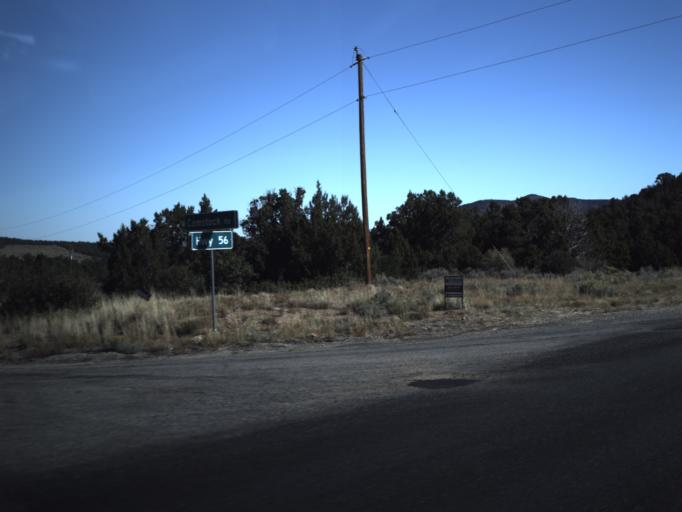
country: US
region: Utah
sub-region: Iron County
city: Cedar City
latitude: 37.6092
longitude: -113.3534
